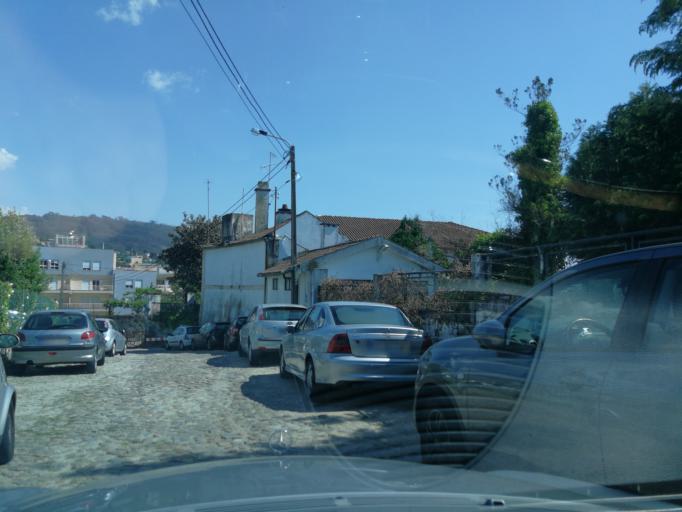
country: PT
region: Braga
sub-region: Braga
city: Braga
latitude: 41.5585
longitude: -8.3999
